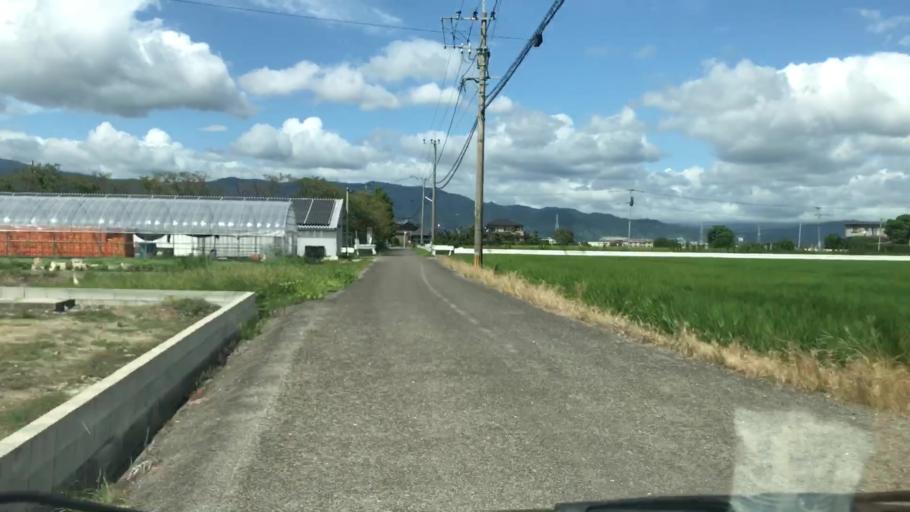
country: JP
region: Saga Prefecture
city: Saga-shi
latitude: 33.2372
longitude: 130.2120
